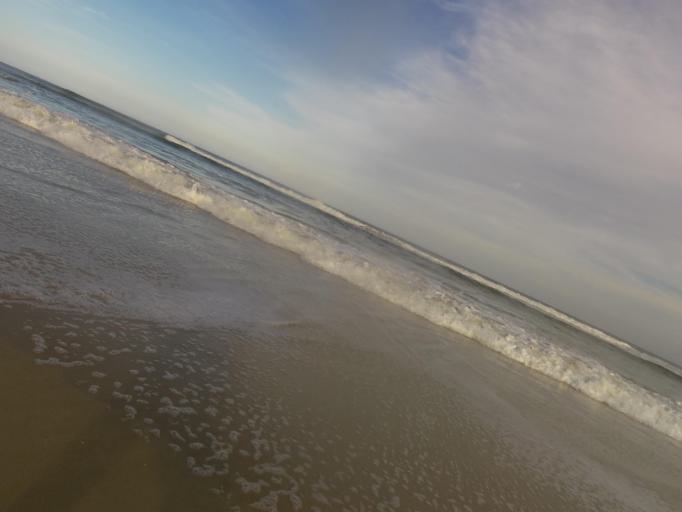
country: US
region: Florida
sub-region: Flagler County
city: Palm Coast
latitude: 29.6237
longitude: -81.1934
